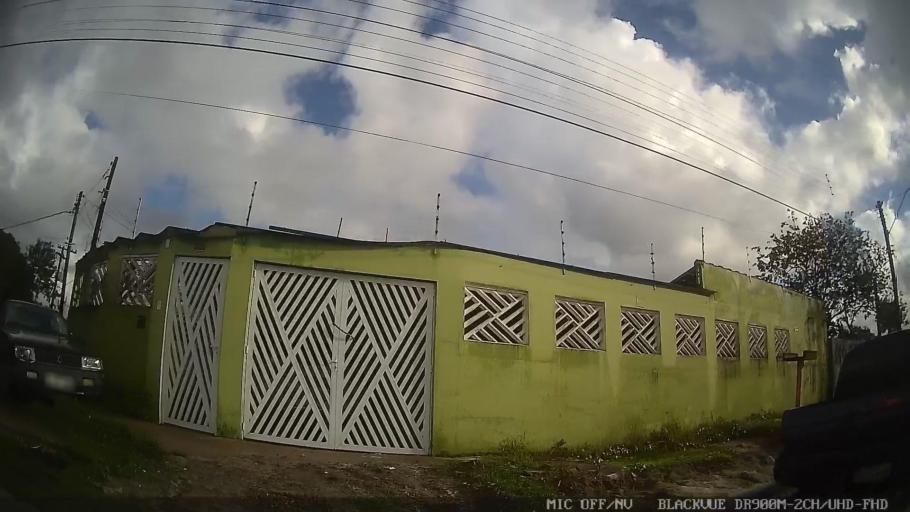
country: BR
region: Sao Paulo
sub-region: Itanhaem
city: Itanhaem
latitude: -24.1761
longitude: -46.8510
